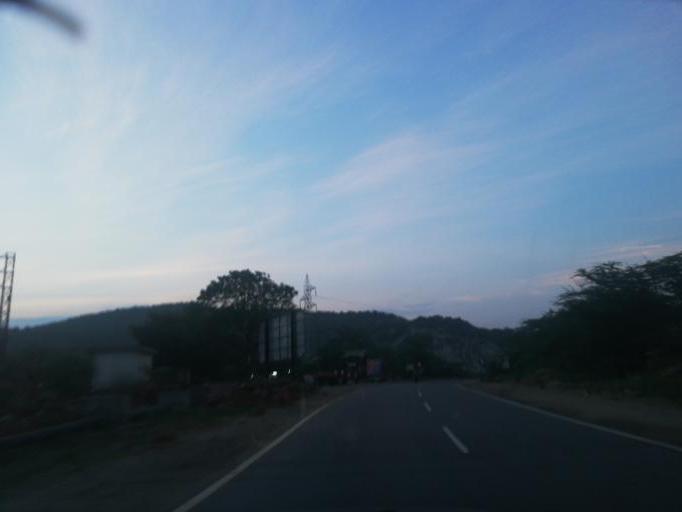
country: IN
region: Andhra Pradesh
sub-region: Guntur
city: Macherla
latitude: 16.6635
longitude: 79.2860
